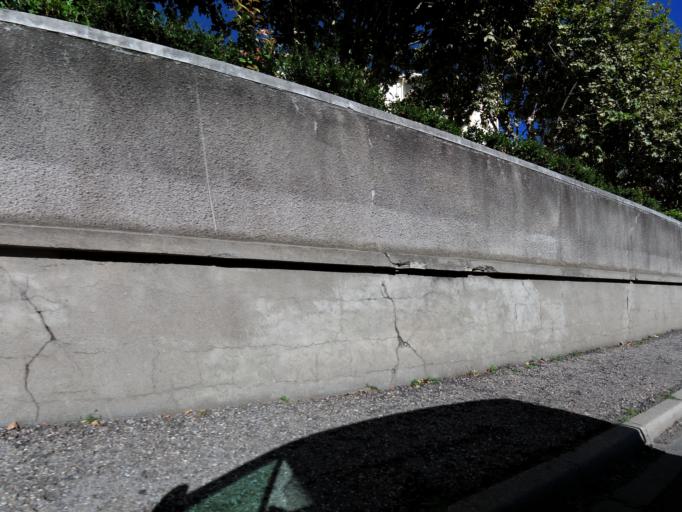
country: FR
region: Languedoc-Roussillon
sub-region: Departement du Gard
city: Nimes
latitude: 43.8238
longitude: 4.3636
